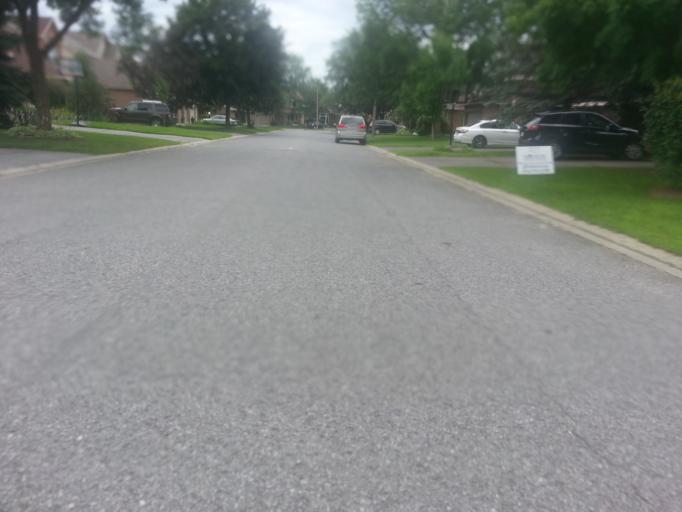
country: CA
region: Ontario
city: Bells Corners
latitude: 45.3296
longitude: -75.9177
